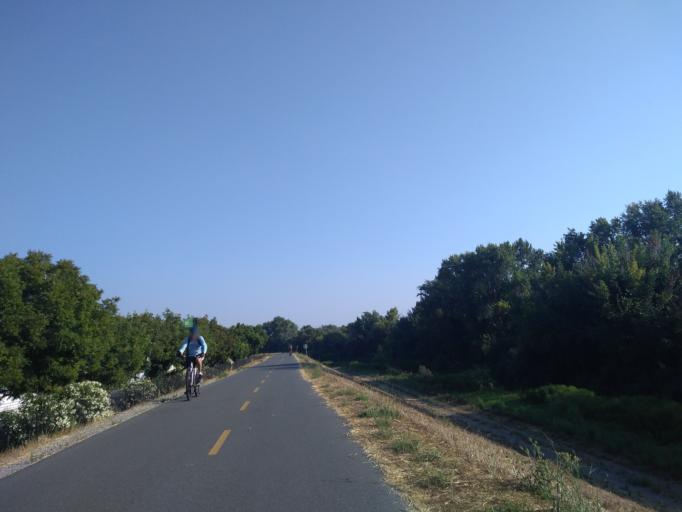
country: US
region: California
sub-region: Santa Clara County
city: Santa Clara
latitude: 37.3923
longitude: -121.9389
